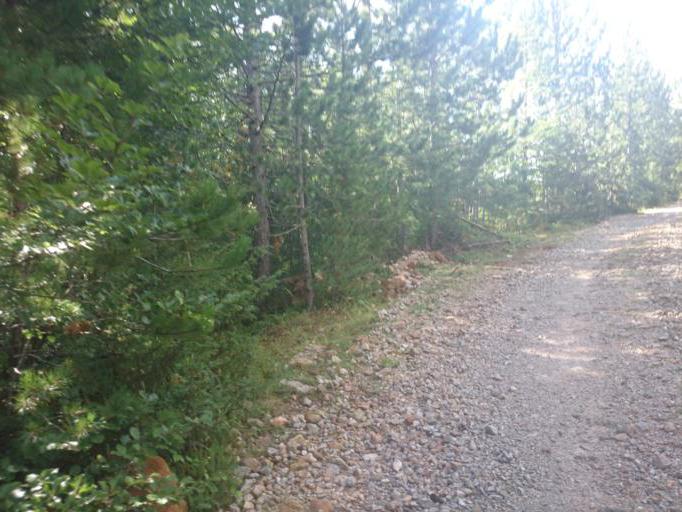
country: AL
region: Diber
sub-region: Rrethi i Dibres
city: Fushe-Lure
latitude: 41.7996
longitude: 20.2094
